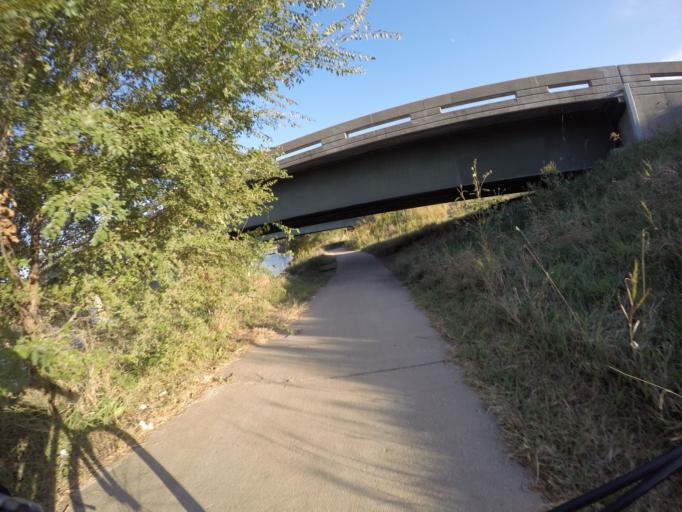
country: US
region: Kansas
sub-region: Riley County
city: Manhattan
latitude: 39.1924
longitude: -96.5386
